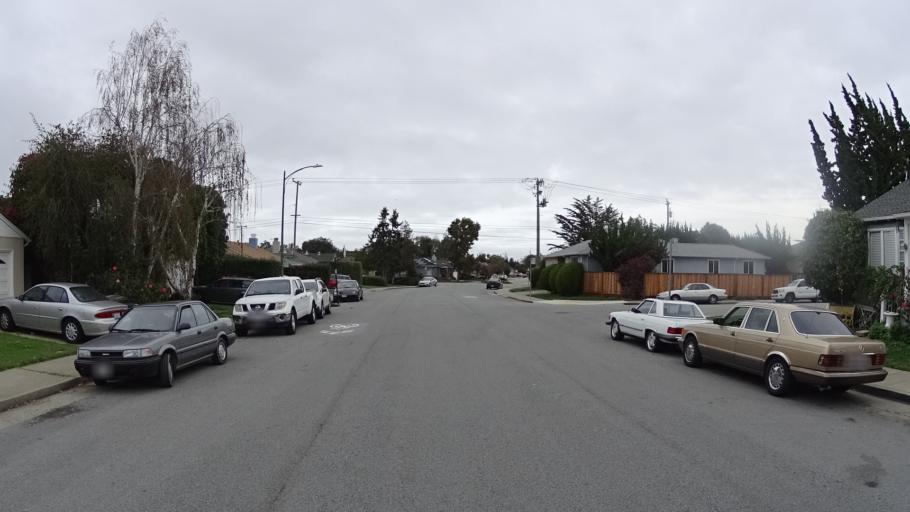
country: US
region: California
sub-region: San Mateo County
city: Belmont
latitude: 37.5371
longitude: -122.2929
